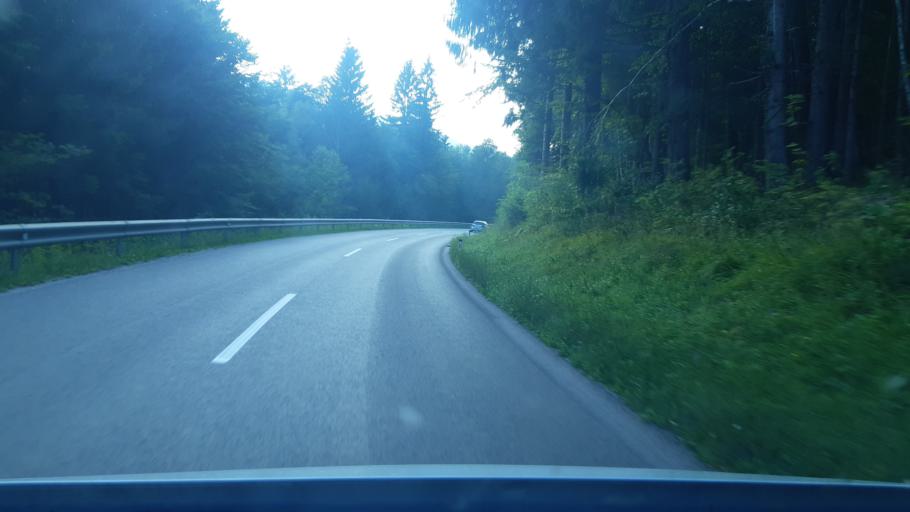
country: SI
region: Semic
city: Semic
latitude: 45.6559
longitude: 15.1196
